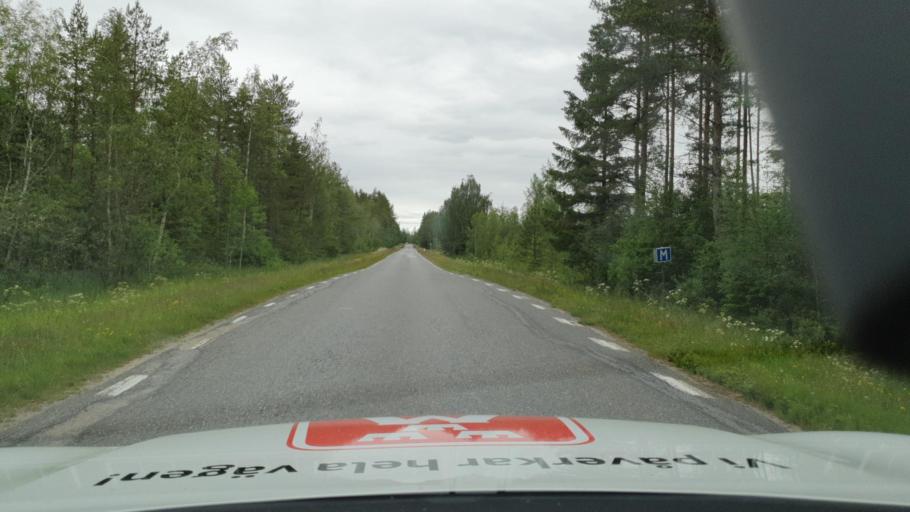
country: SE
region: Vaesterbotten
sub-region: Nordmalings Kommun
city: Nordmaling
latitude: 63.4907
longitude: 19.4378
